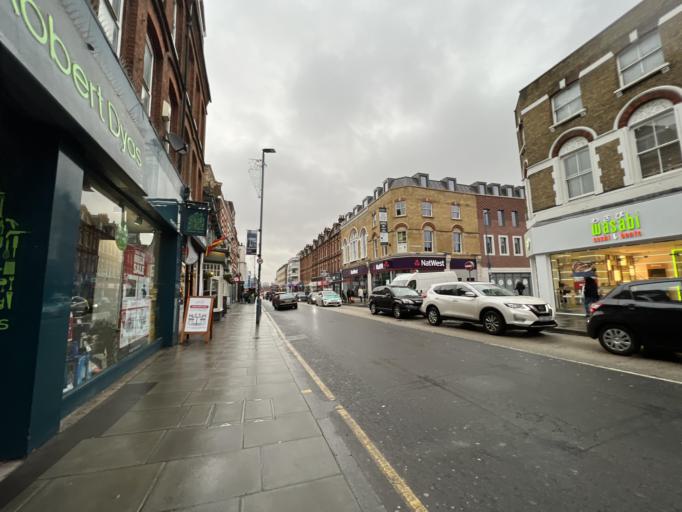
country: GB
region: England
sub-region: Greater London
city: Wandsworth
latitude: 51.4624
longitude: -0.2162
